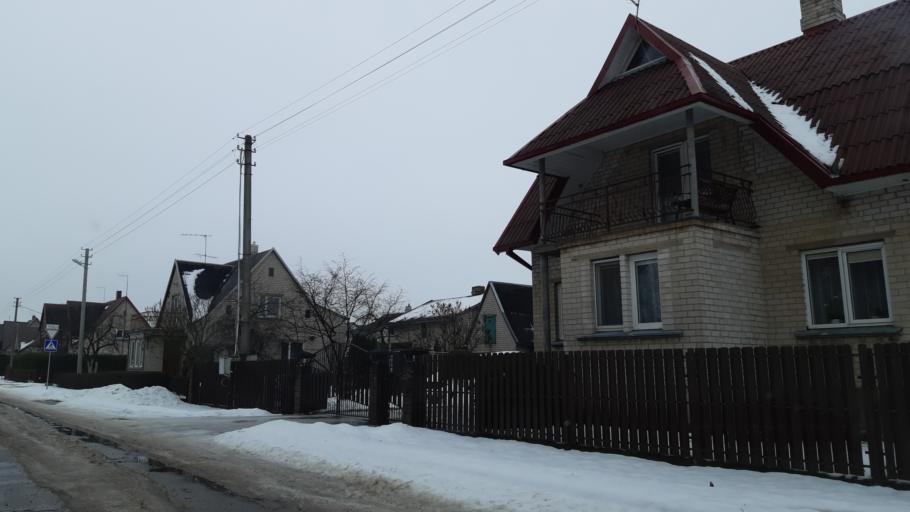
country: LT
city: Vilkaviskis
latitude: 54.6458
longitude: 23.0329
